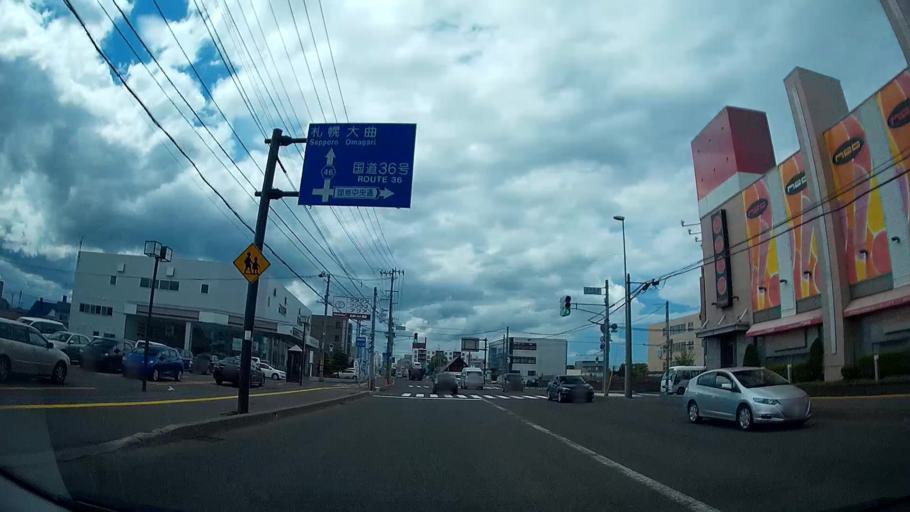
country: JP
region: Hokkaido
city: Chitose
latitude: 42.8764
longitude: 141.5826
